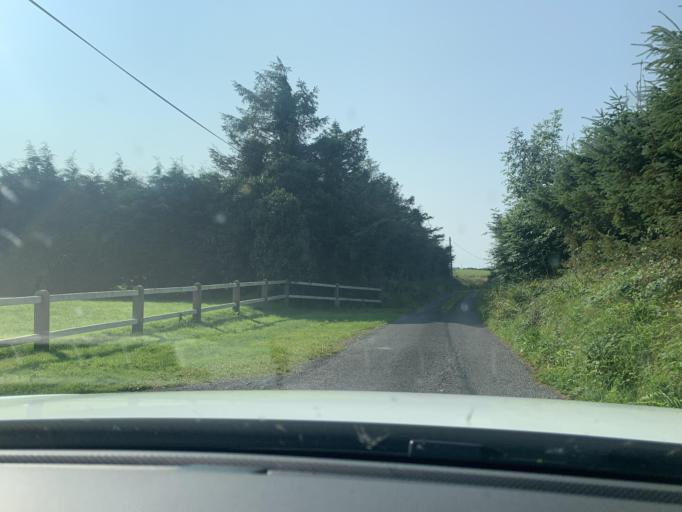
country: IE
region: Connaught
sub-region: Maigh Eo
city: Ballyhaunis
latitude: 53.7894
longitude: -8.7386
